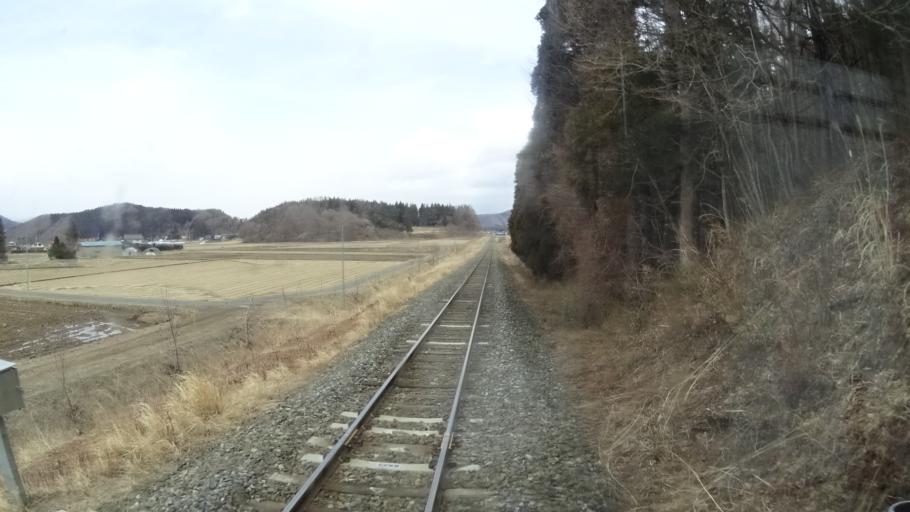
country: JP
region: Iwate
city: Tono
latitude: 39.2720
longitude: 141.5897
